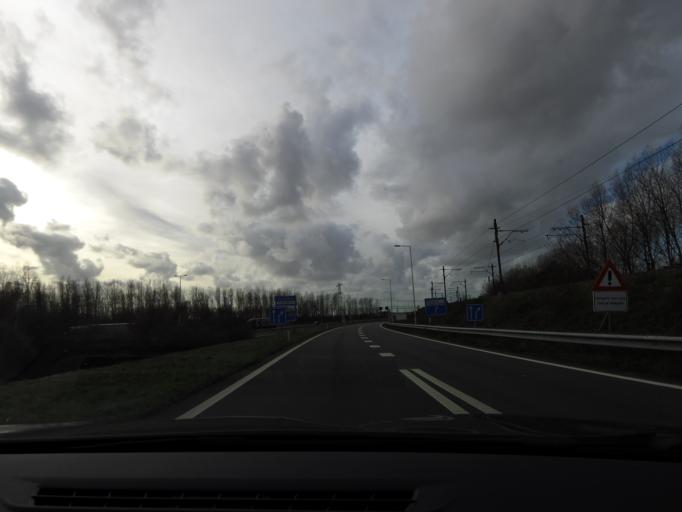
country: NL
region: South Holland
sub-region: Gemeente Rotterdam
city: Hoek van Holland
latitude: 51.9327
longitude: 4.1012
